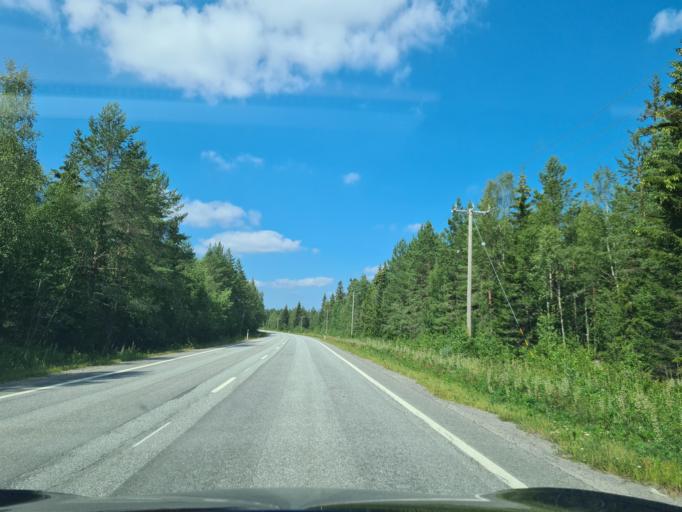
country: FI
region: Ostrobothnia
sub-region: Vaasa
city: Vaasa
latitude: 63.1767
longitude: 21.5768
